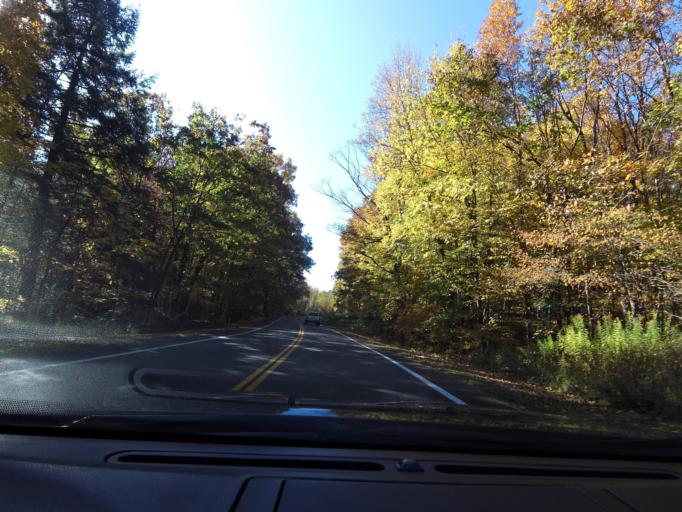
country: US
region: New York
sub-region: Wyoming County
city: Perry
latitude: 42.6510
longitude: -77.9825
